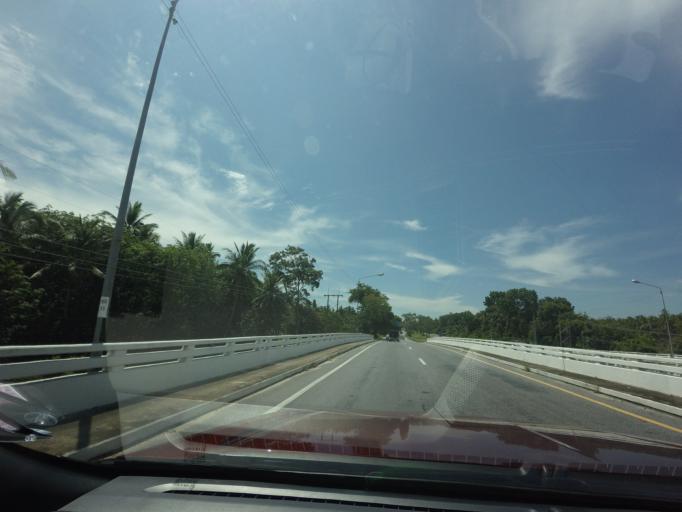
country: TH
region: Pattani
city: Mai Kaen
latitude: 6.6262
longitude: 101.6294
